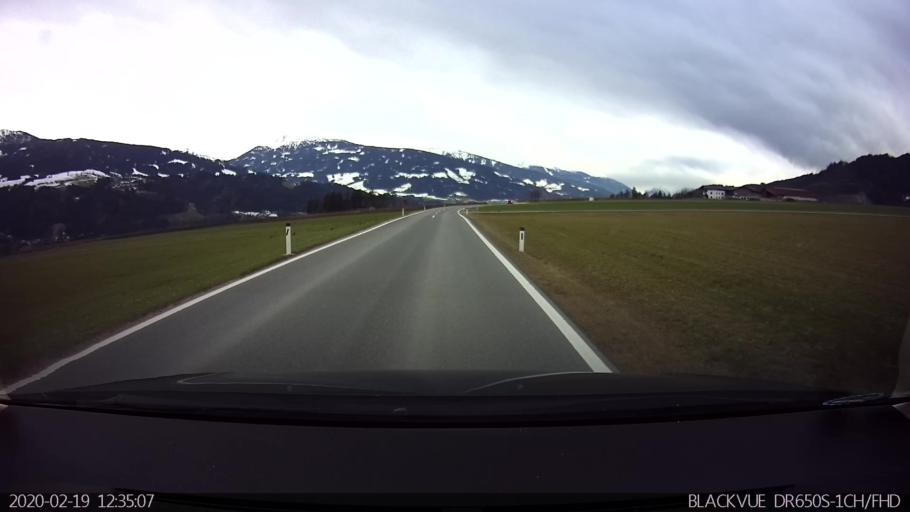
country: AT
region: Tyrol
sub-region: Politischer Bezirk Schwaz
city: Vomp
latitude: 47.3363
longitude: 11.6755
